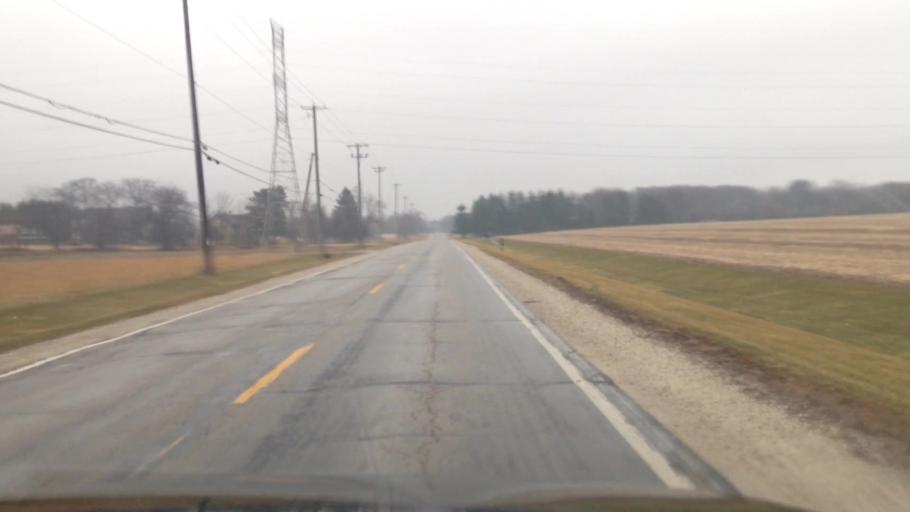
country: US
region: Wisconsin
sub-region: Washington County
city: Richfield
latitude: 43.2502
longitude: -88.1550
